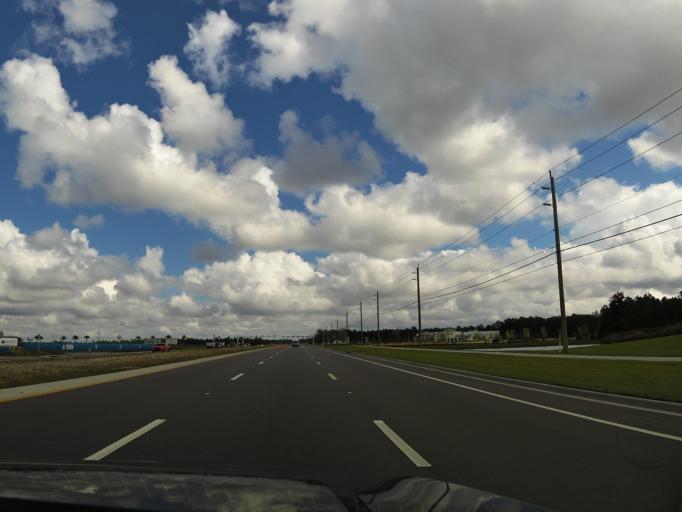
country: US
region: Florida
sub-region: Saint Johns County
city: Palm Valley
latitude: 30.0775
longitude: -81.4818
